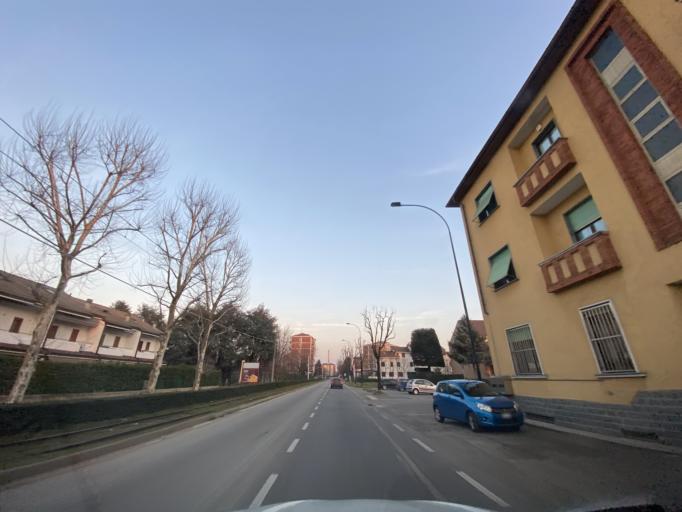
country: IT
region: Lombardy
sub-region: Provincia di Monza e Brianza
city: Limbiate
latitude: 45.5983
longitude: 9.1365
